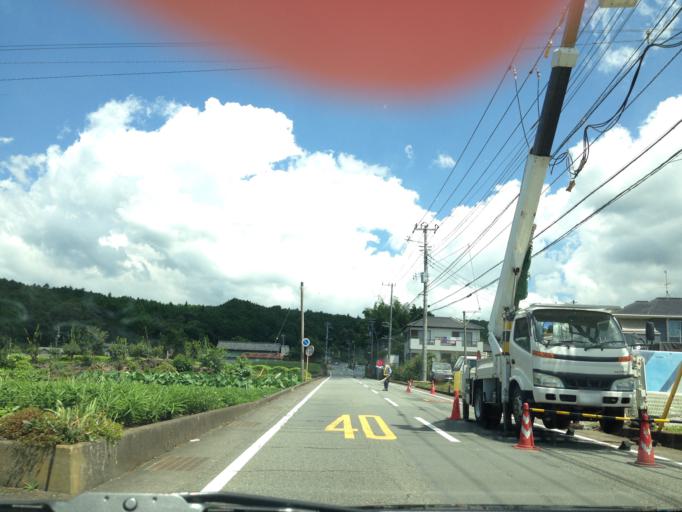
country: JP
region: Shizuoka
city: Fuji
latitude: 35.2051
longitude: 138.7225
